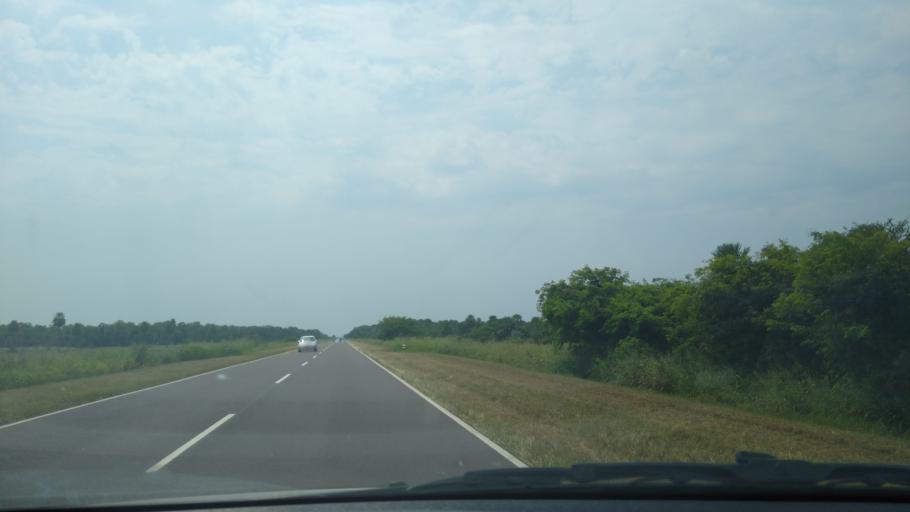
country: AR
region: Chaco
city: La Eduvigis
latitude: -27.0204
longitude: -58.9682
